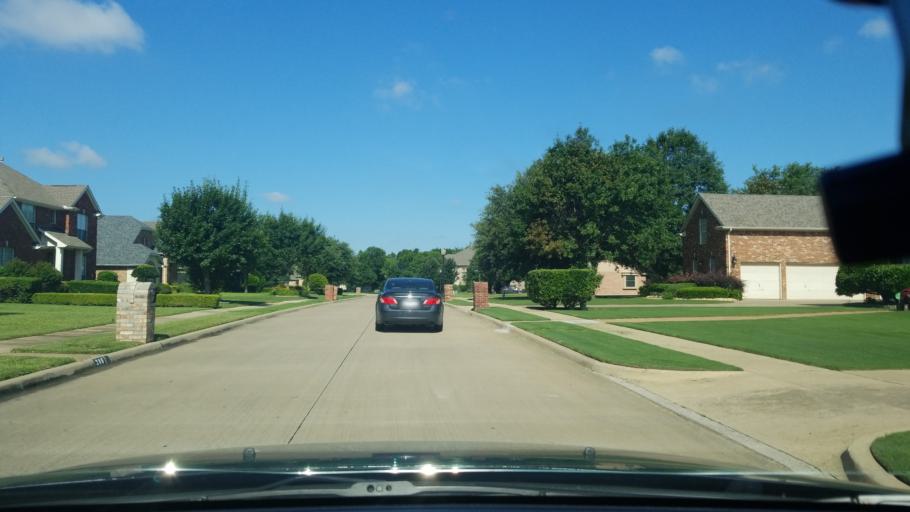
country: US
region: Texas
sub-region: Dallas County
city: Sunnyvale
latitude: 32.8078
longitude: -96.5859
